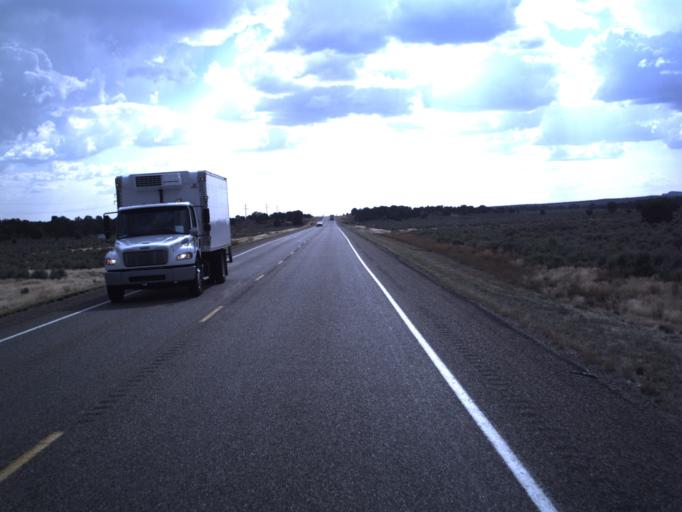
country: US
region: Utah
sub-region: Kane County
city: Kanab
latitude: 37.1106
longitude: -112.1179
